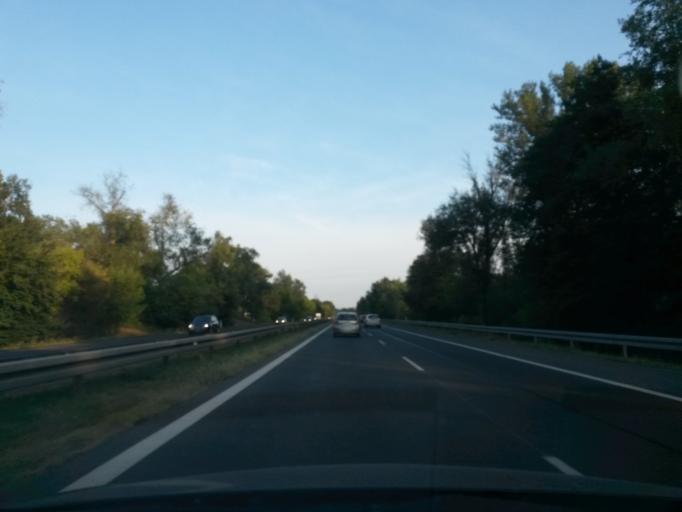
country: PL
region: Masovian Voivodeship
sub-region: Powiat nowodworski
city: Nowy Dwor Mazowiecki
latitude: 52.4034
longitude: 20.7075
